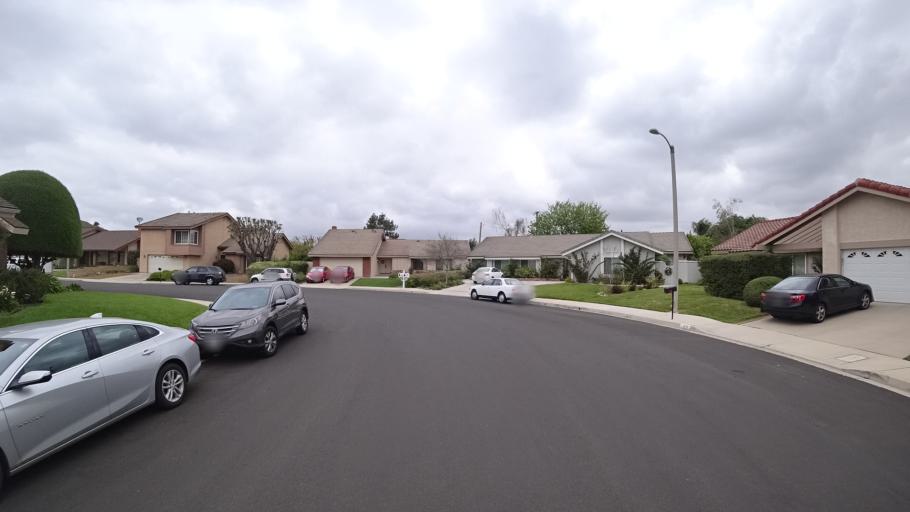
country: US
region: California
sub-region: Ventura County
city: Thousand Oaks
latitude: 34.2198
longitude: -118.8808
